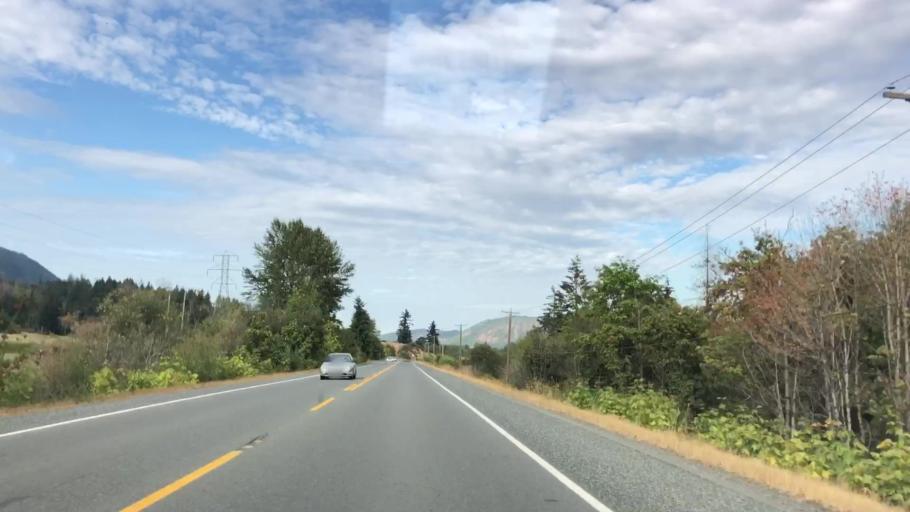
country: CA
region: British Columbia
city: Duncan
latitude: 48.8088
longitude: -123.7525
